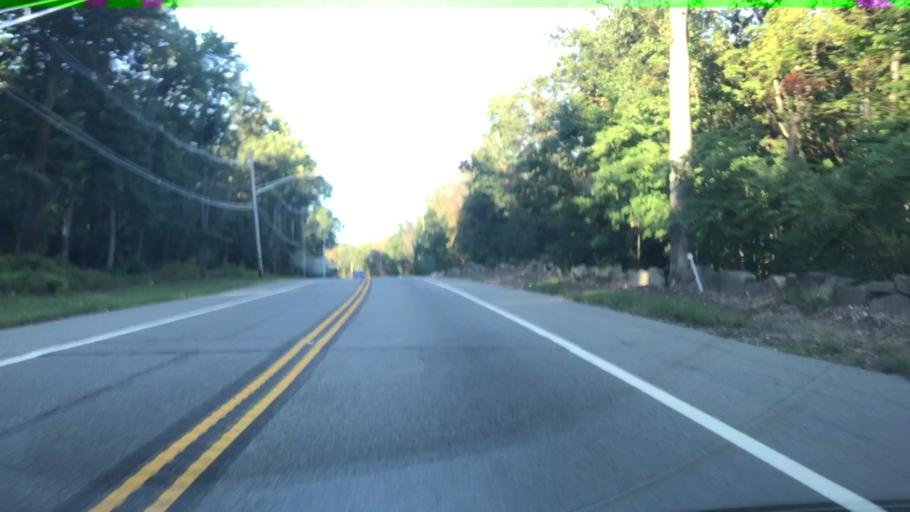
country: US
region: New Jersey
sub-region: Bergen County
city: Tenafly
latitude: 40.9236
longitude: -73.9325
